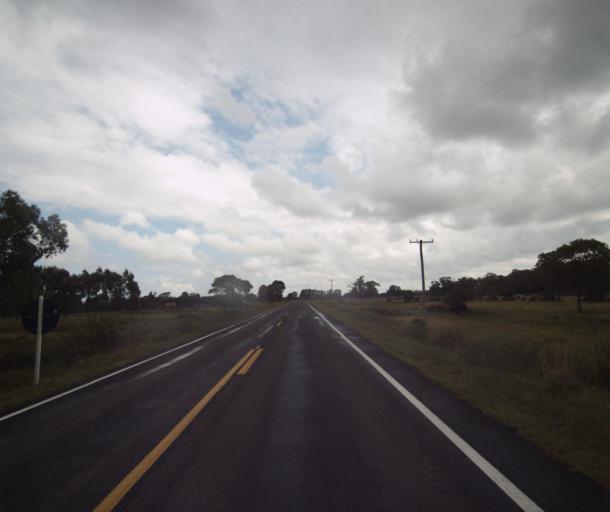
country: BR
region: Rio Grande do Sul
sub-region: Tapes
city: Tapes
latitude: -31.3180
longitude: -51.1211
